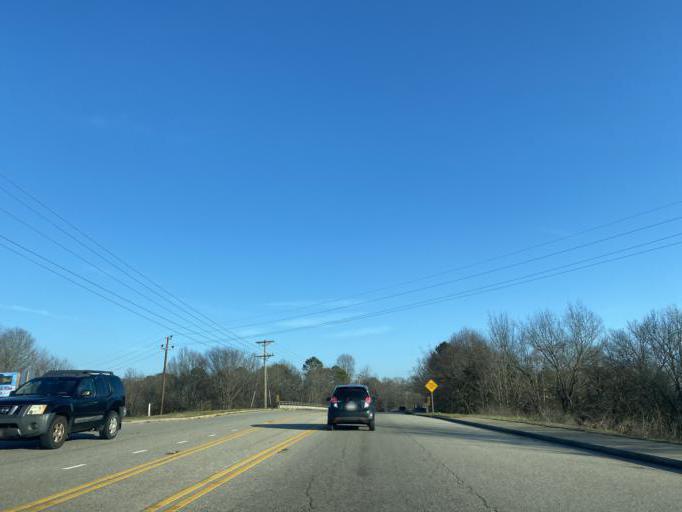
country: US
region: South Carolina
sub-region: Cherokee County
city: Gaffney
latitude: 35.0647
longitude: -81.6629
